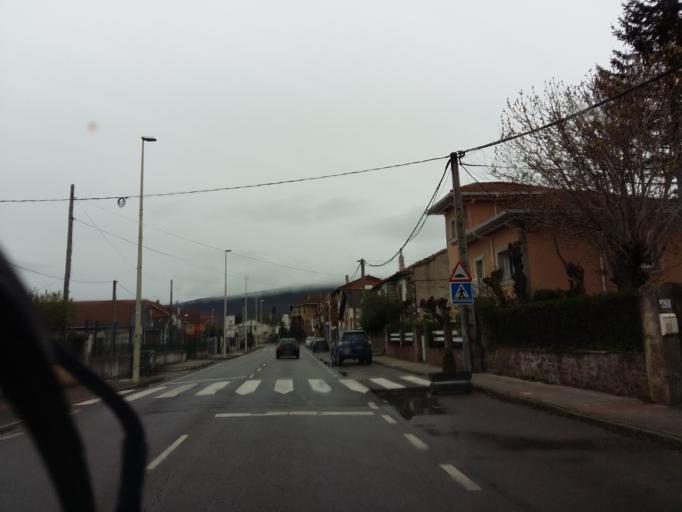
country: ES
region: Cantabria
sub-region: Provincia de Cantabria
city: Reinosa
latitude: 42.9828
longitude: -4.1482
